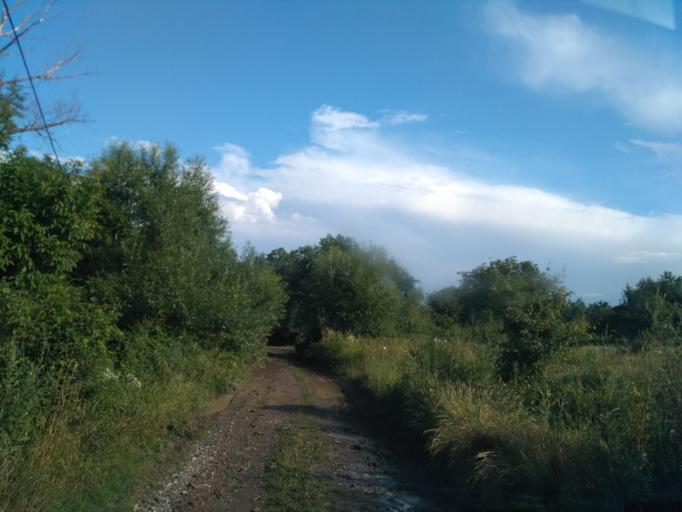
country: SK
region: Kosicky
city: Secovce
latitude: 48.6009
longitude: 21.5513
